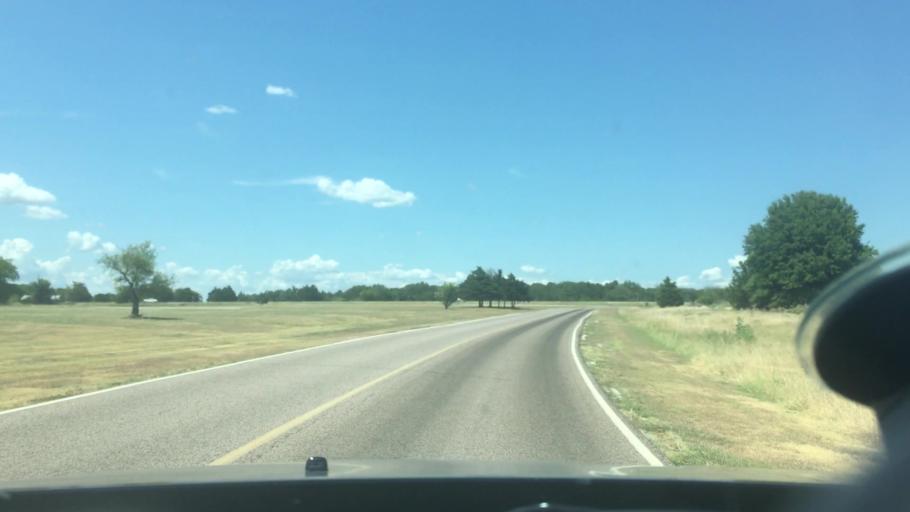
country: US
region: Oklahoma
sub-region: Marshall County
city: Kingston
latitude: 33.9937
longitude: -96.6416
